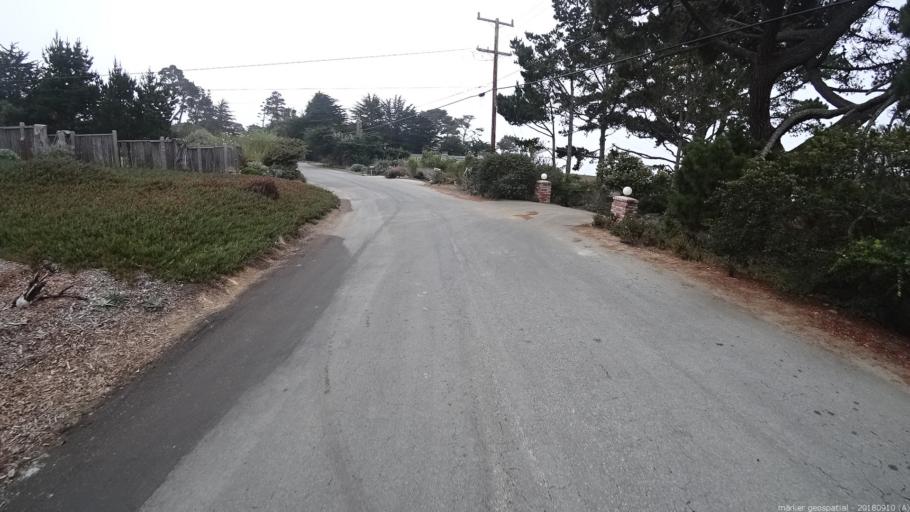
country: US
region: California
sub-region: Monterey County
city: Carmel-by-the-Sea
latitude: 36.4890
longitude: -121.9402
